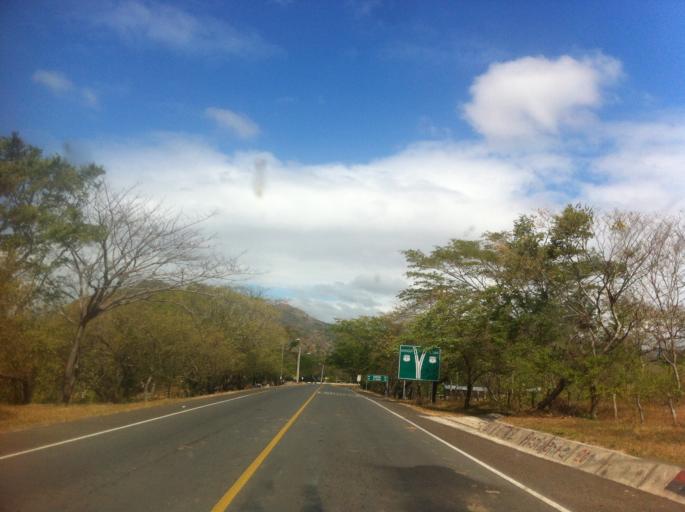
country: NI
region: Chontales
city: Acoyapa
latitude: 11.9989
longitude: -85.1614
